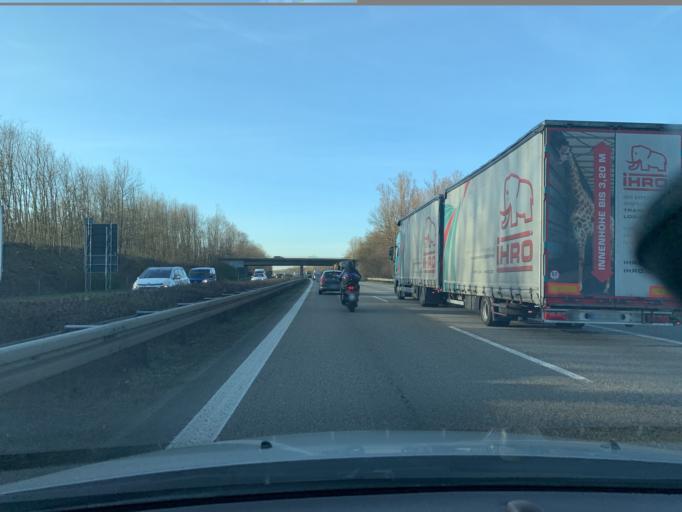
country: DE
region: Baden-Wuerttemberg
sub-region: Freiburg Region
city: Vorstetten
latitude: 48.0714
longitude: 7.8098
